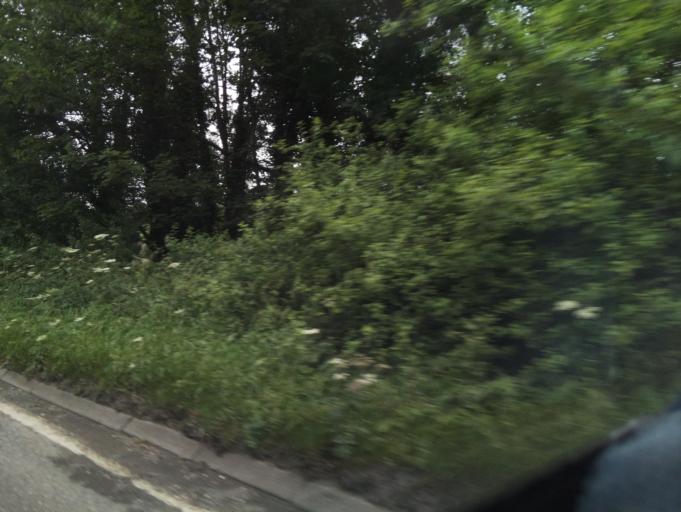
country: GB
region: England
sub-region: Staffordshire
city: Mayfield
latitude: 52.9974
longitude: -1.7501
